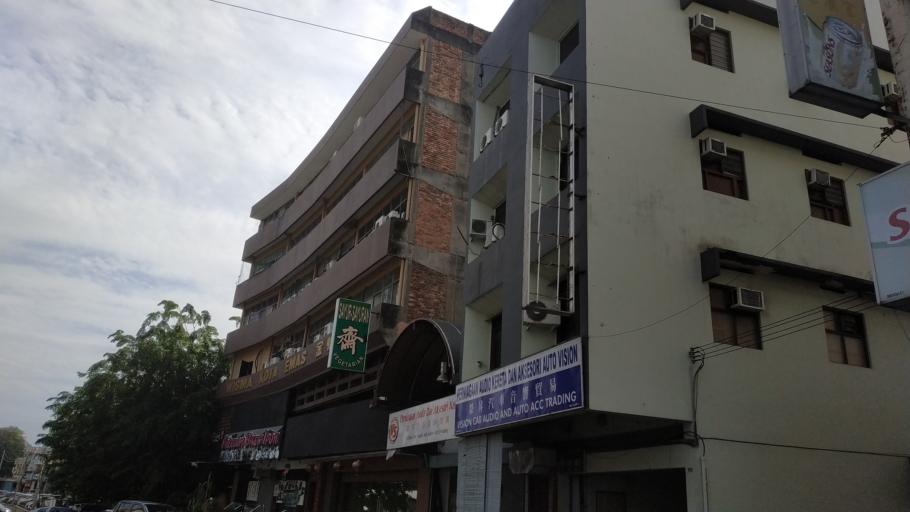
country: MY
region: Perak
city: Ipoh
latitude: 4.5902
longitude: 101.0835
